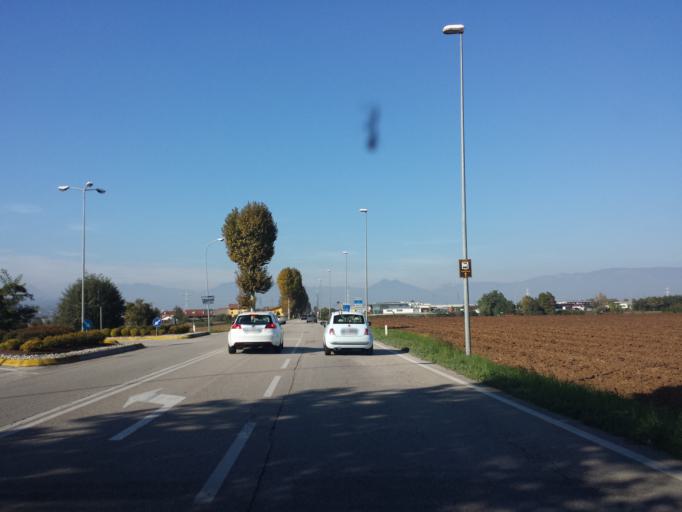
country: IT
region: Veneto
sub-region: Provincia di Vicenza
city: Crispi Cavour
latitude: 45.5815
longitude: 11.5068
